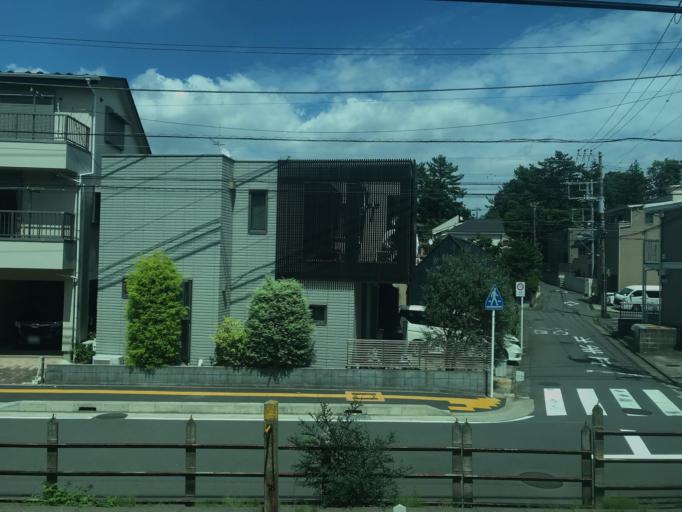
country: JP
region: Kanagawa
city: Fujisawa
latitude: 35.3802
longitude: 139.4720
